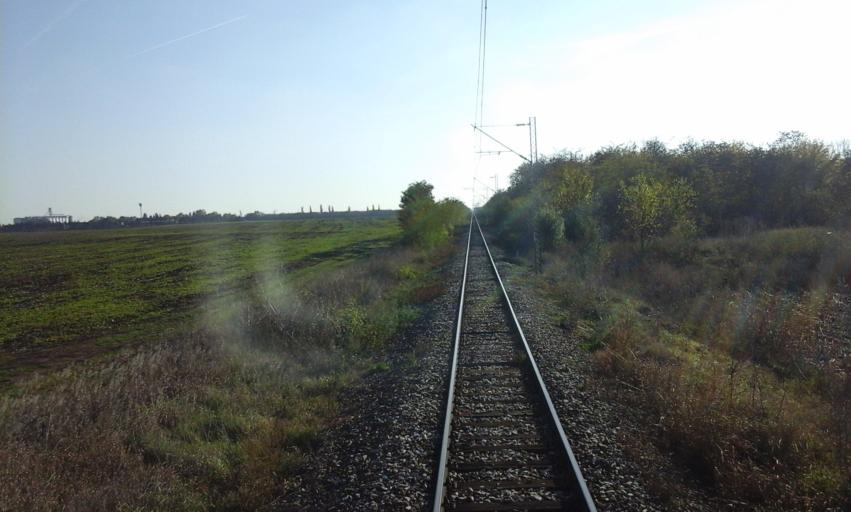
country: RS
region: Autonomna Pokrajina Vojvodina
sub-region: Severnobacki Okrug
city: Backa Topola
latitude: 45.7871
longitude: 19.6476
